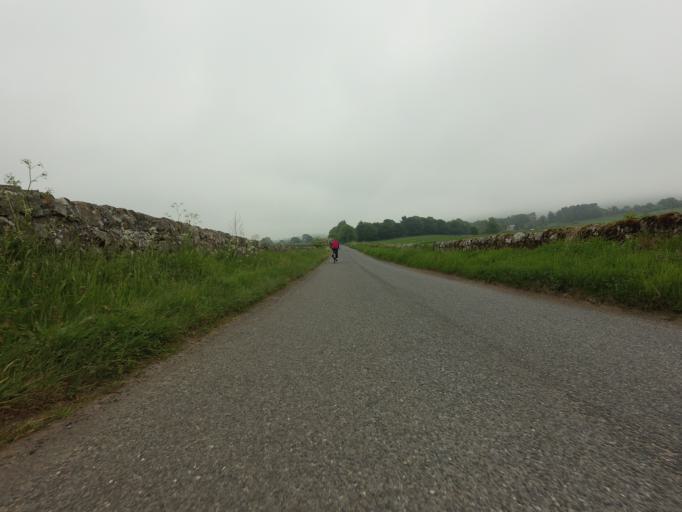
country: GB
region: Scotland
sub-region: Perth and Kinross
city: Kinross
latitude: 56.1655
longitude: -3.4539
